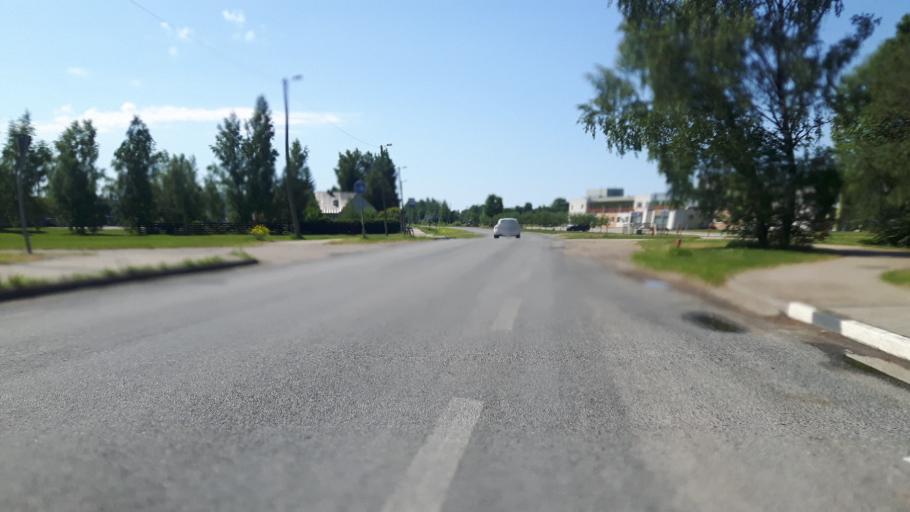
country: EE
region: Paernumaa
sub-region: Vaendra vald (alev)
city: Vandra
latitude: 58.6470
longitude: 25.0299
